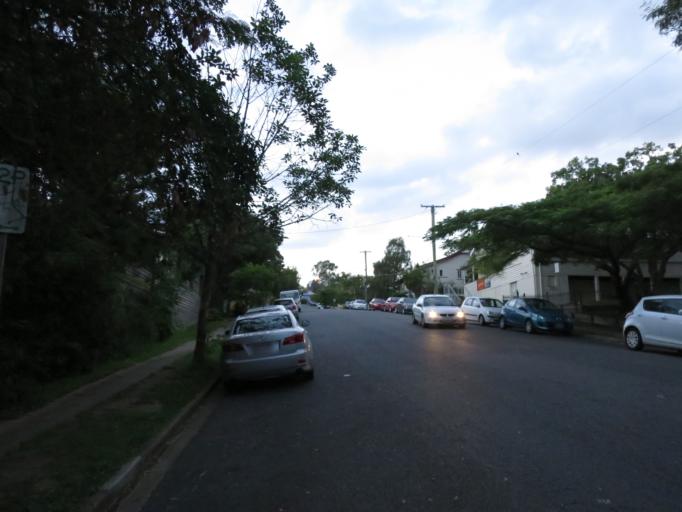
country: AU
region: Queensland
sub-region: Brisbane
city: Milton
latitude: -27.4619
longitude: 153.0099
